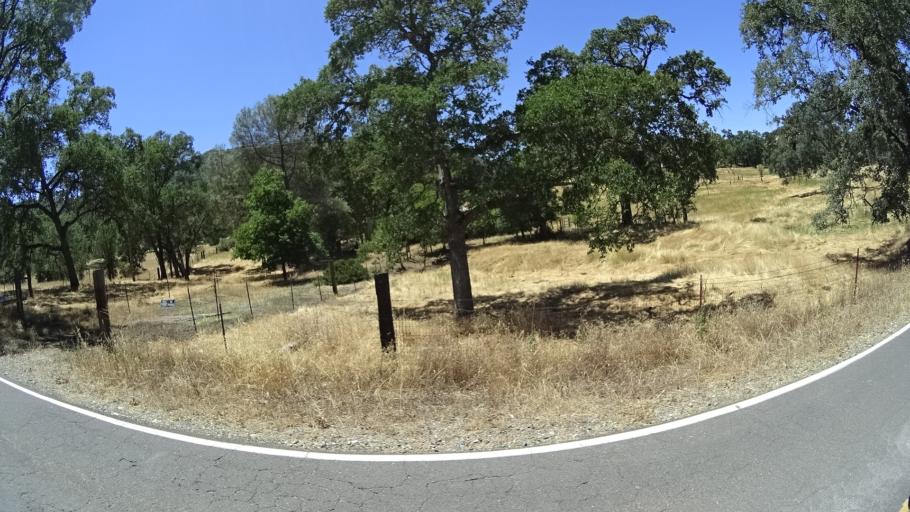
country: US
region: California
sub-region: Calaveras County
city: Copperopolis
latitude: 38.0764
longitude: -120.6653
